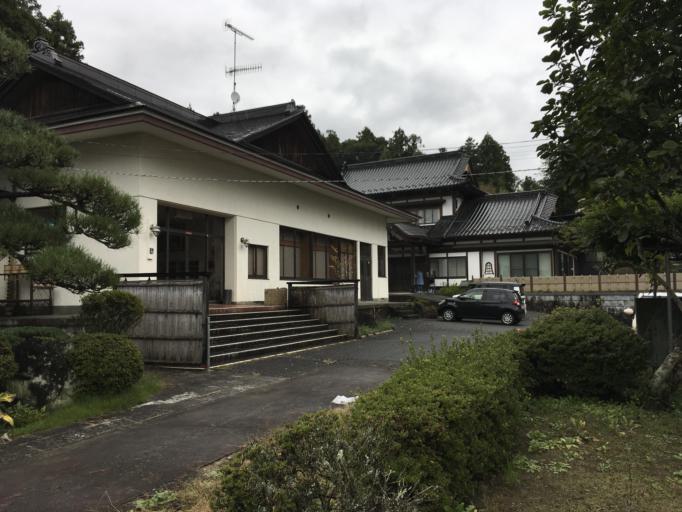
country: JP
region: Iwate
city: Ichinoseki
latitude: 38.8499
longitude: 141.1767
